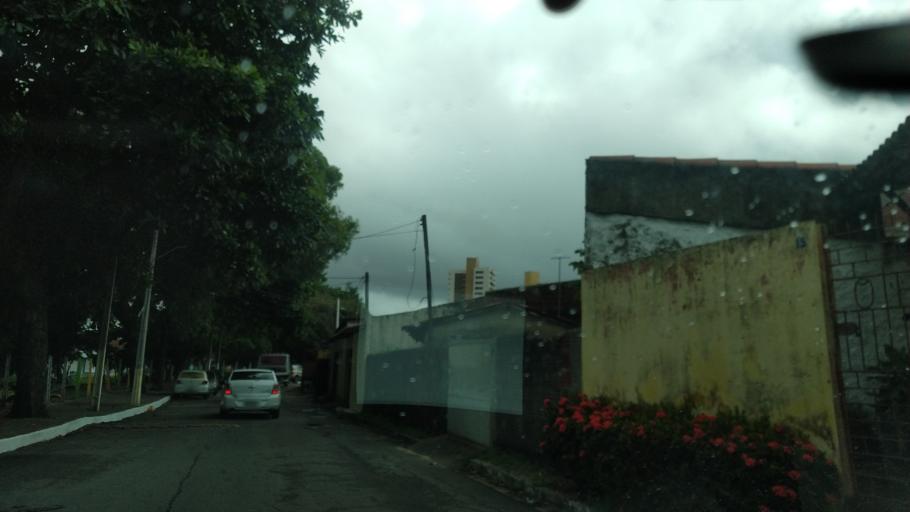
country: BR
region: Rio Grande do Norte
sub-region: Natal
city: Natal
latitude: -5.8624
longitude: -35.2092
